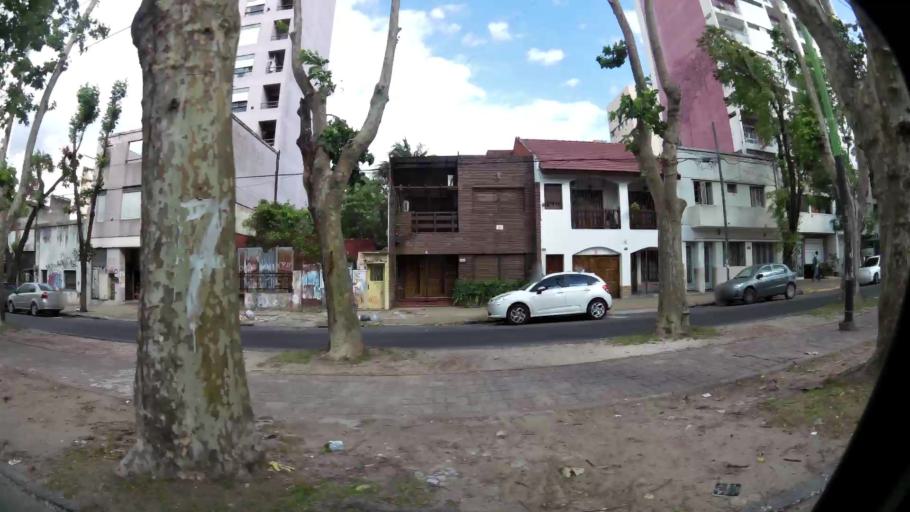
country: AR
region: Buenos Aires
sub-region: Partido de La Plata
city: La Plata
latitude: -34.9177
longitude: -57.9381
